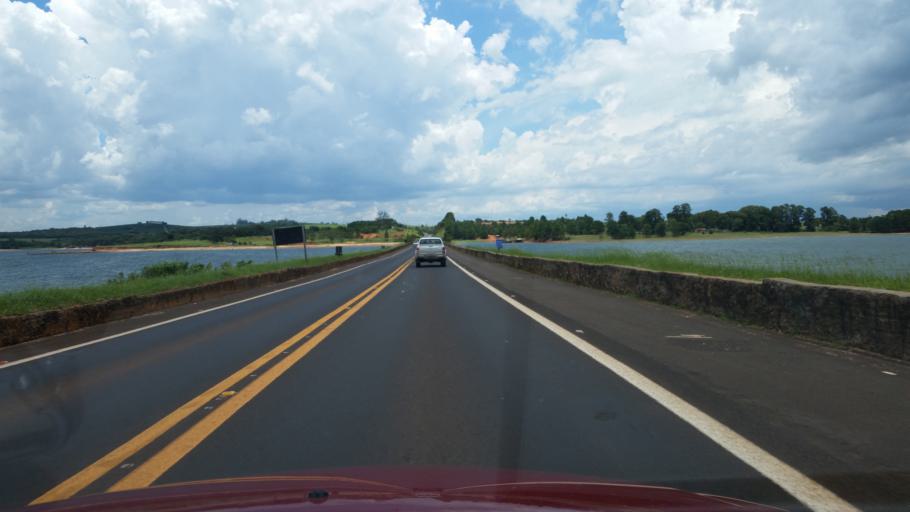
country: BR
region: Sao Paulo
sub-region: Itai
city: Itai
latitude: -23.2689
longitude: -49.0104
